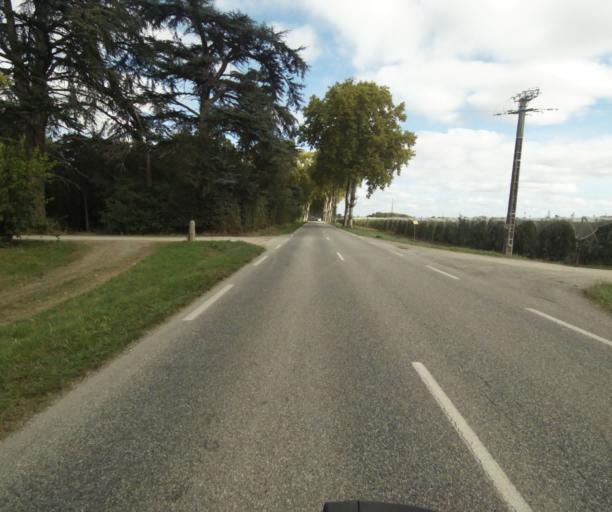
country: FR
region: Midi-Pyrenees
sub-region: Departement du Tarn-et-Garonne
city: Montech
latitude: 43.9532
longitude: 1.1862
